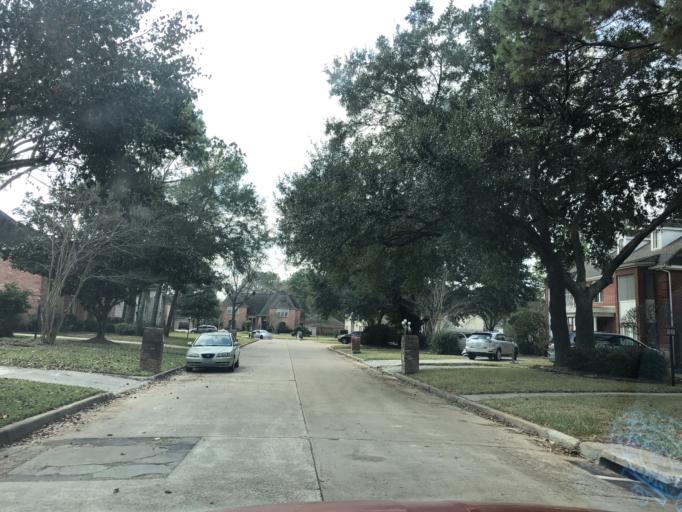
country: US
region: Texas
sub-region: Harris County
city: Tomball
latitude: 30.0260
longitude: -95.5430
